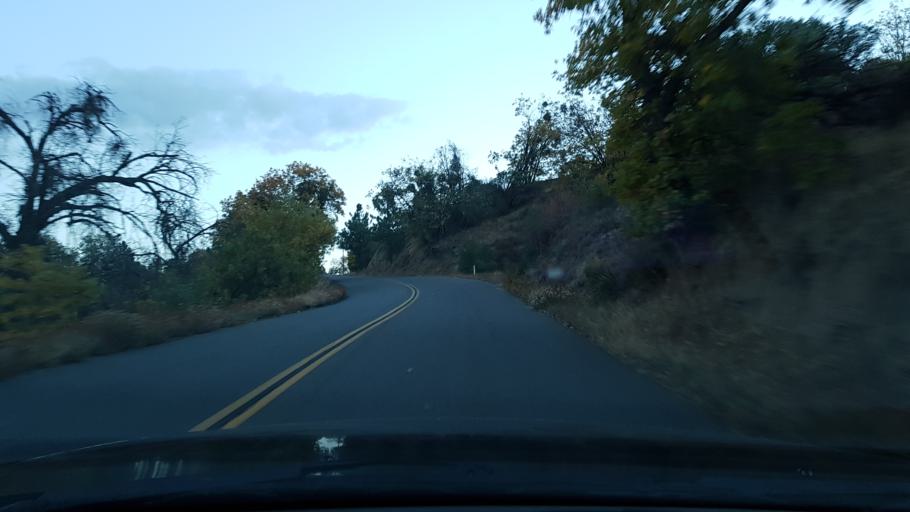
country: US
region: California
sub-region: San Diego County
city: Julian
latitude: 33.1102
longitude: -116.6031
